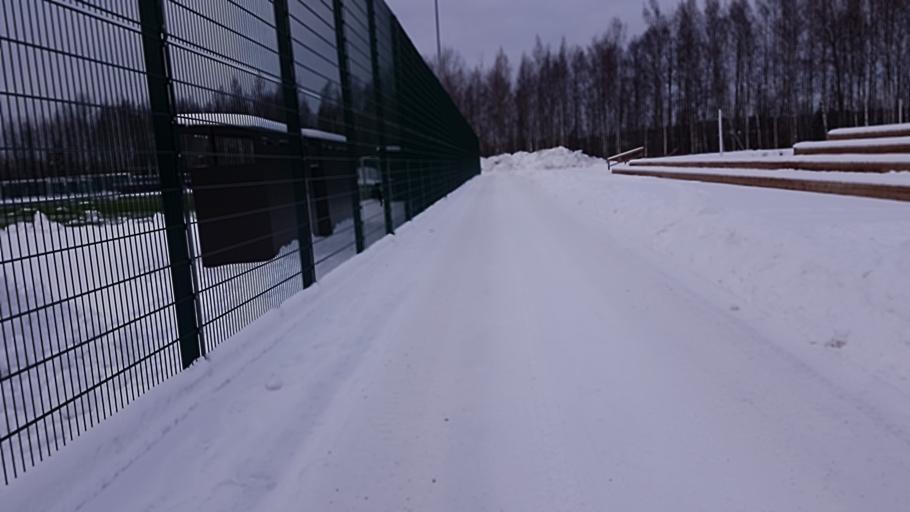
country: FI
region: Uusimaa
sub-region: Helsinki
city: Espoo
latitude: 60.2107
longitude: 24.6741
